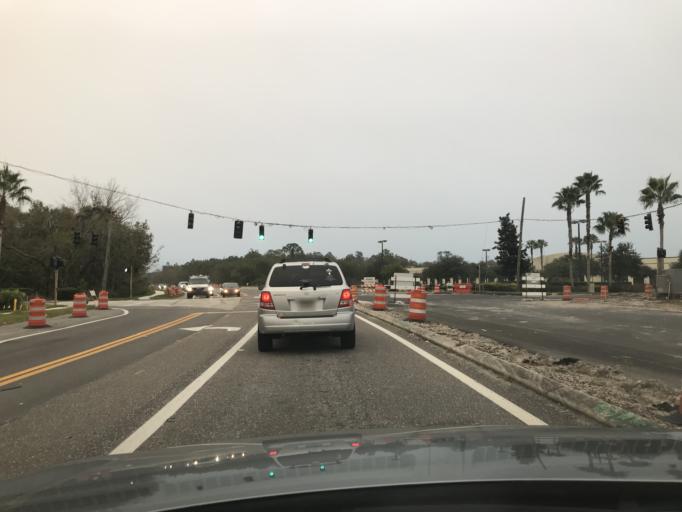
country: US
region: Florida
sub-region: Pinellas County
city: Oldsmar
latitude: 28.0512
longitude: -82.6573
